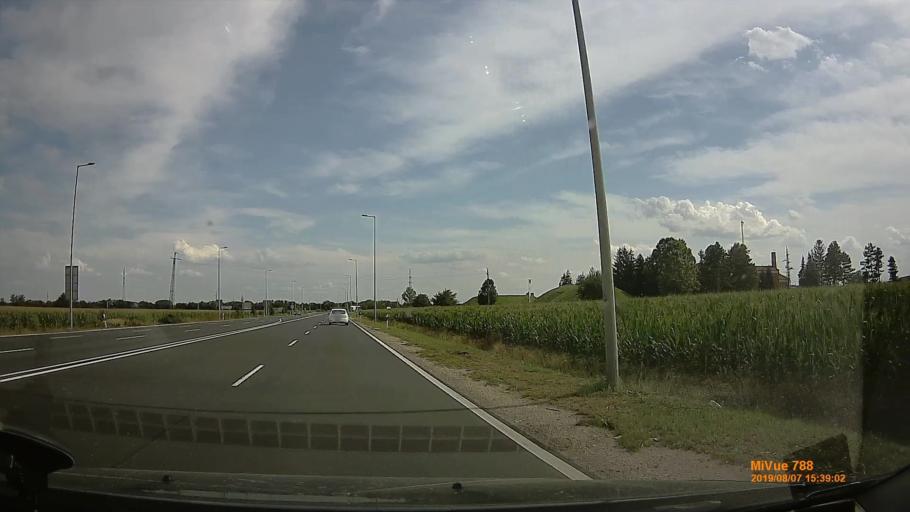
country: HU
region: Vas
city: Szombathely
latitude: 47.2263
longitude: 16.6566
